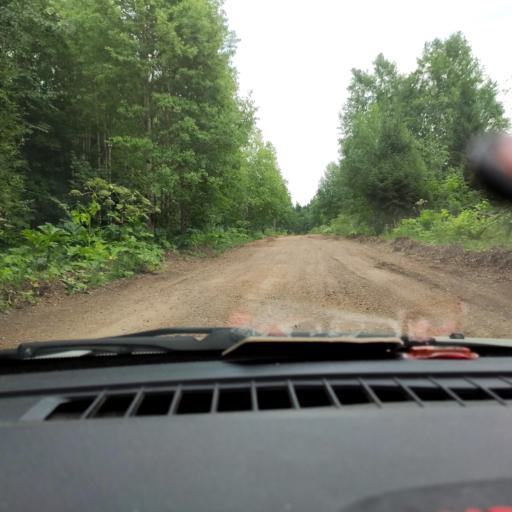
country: RU
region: Perm
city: Kultayevo
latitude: 57.8170
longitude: 56.0005
